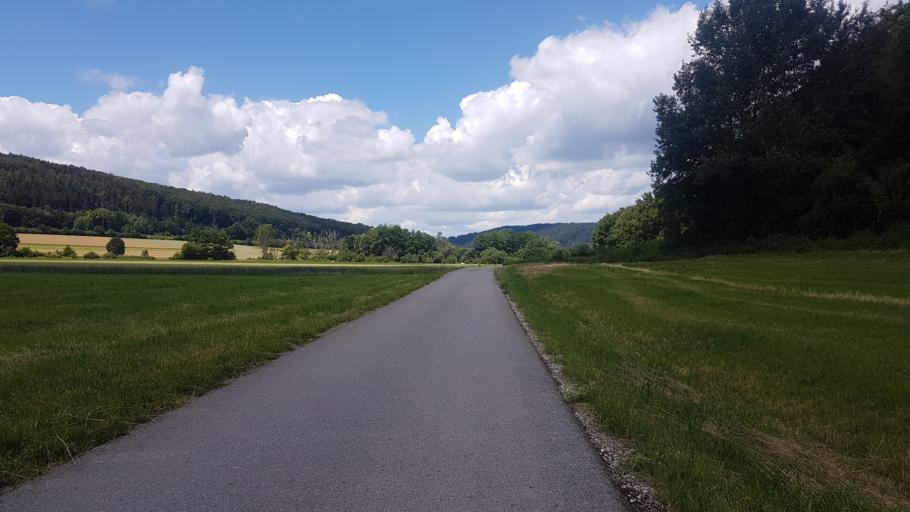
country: DE
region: Bavaria
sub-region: Upper Bavaria
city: Eichstaett
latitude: 48.8832
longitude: 11.1472
